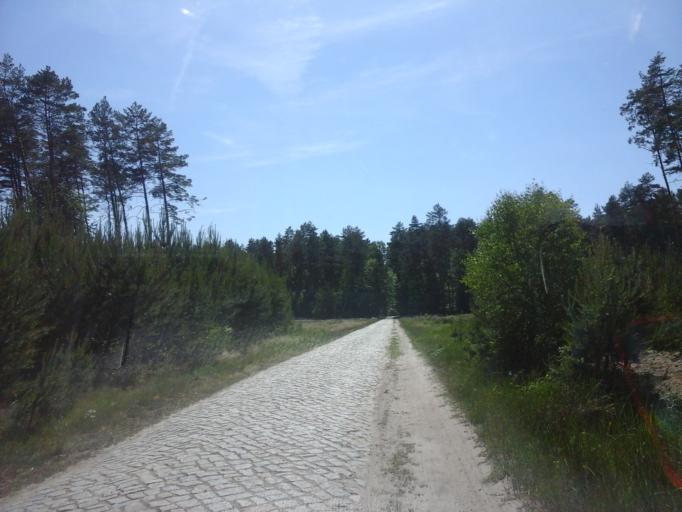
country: PL
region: West Pomeranian Voivodeship
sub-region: Powiat choszczenski
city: Drawno
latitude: 53.1179
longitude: 15.8047
